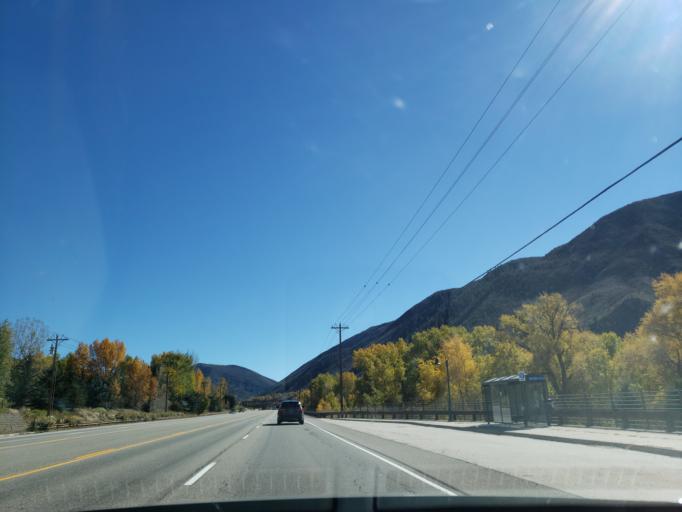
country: US
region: Colorado
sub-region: Eagle County
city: Basalt
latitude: 39.3505
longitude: -107.0166
